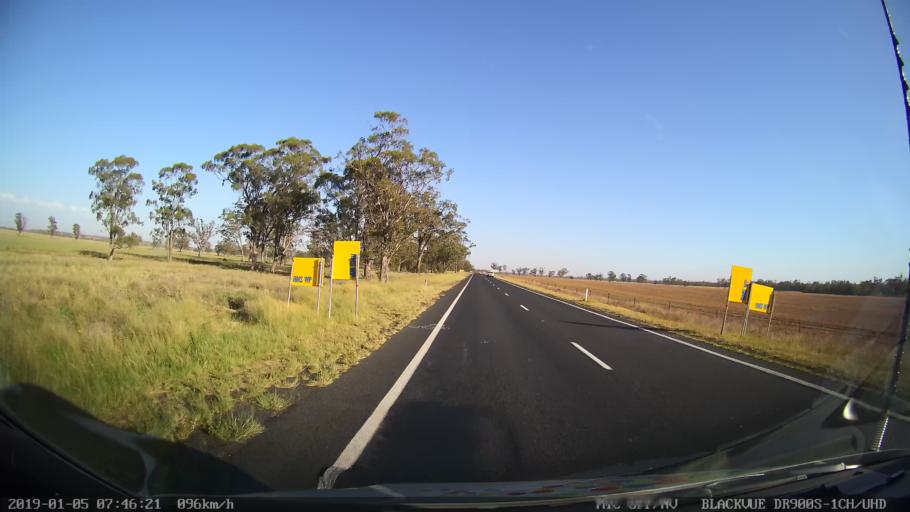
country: AU
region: New South Wales
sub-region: Gilgandra
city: Gilgandra
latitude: -31.8455
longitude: 148.6437
